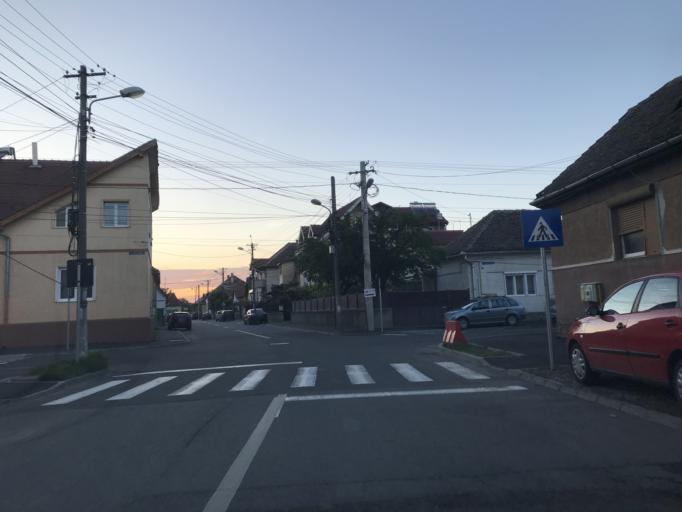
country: RO
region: Sibiu
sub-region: Municipiul Sibiu
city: Sibiu
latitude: 45.8024
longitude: 24.1657
